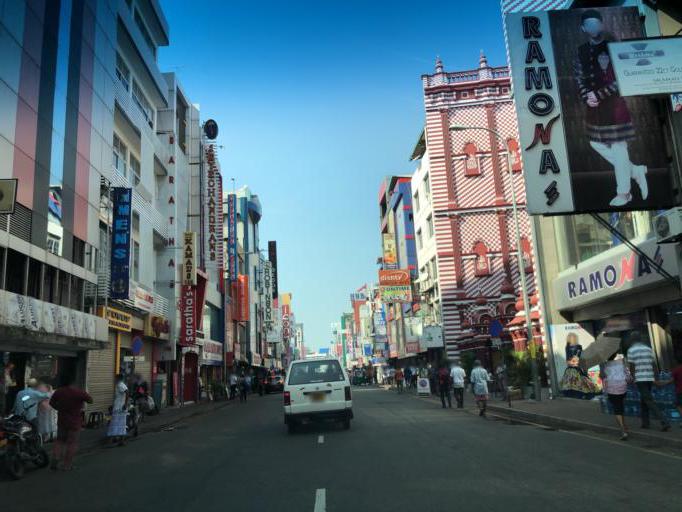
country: LK
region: Western
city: Colombo
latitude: 6.9383
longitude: 79.8525
